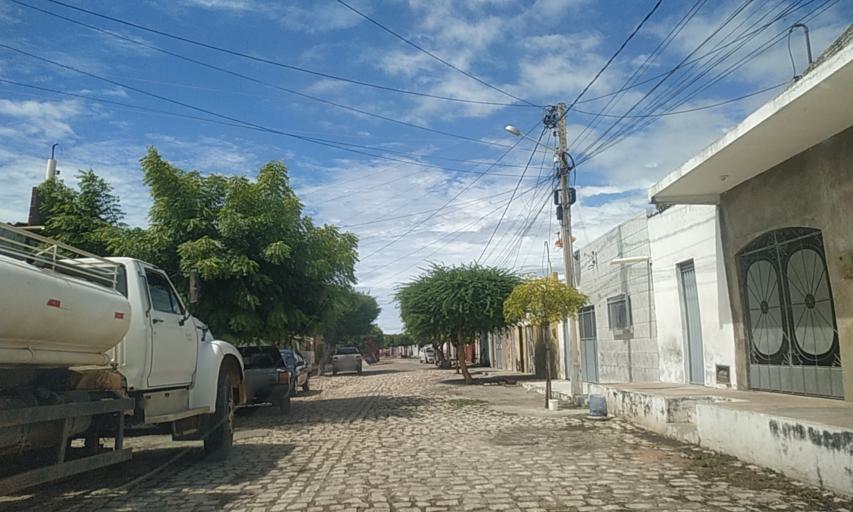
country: BR
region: Rio Grande do Norte
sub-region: Areia Branca
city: Areia Branca
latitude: -4.9492
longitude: -37.1273
